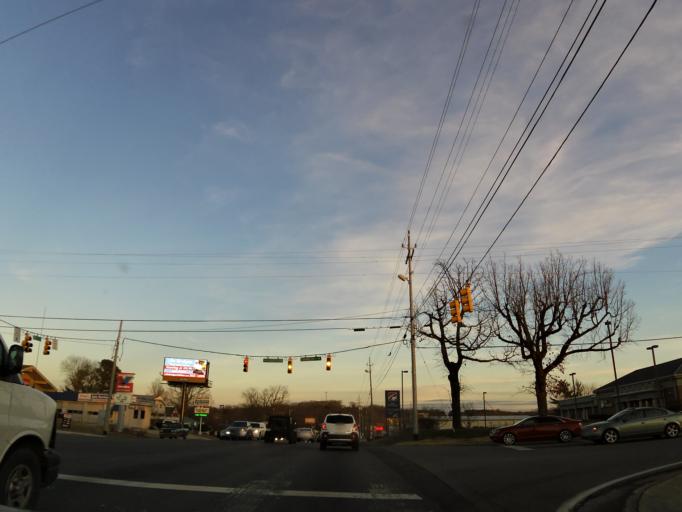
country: US
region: Tennessee
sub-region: Bradley County
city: East Cleveland
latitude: 35.1794
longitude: -84.8676
